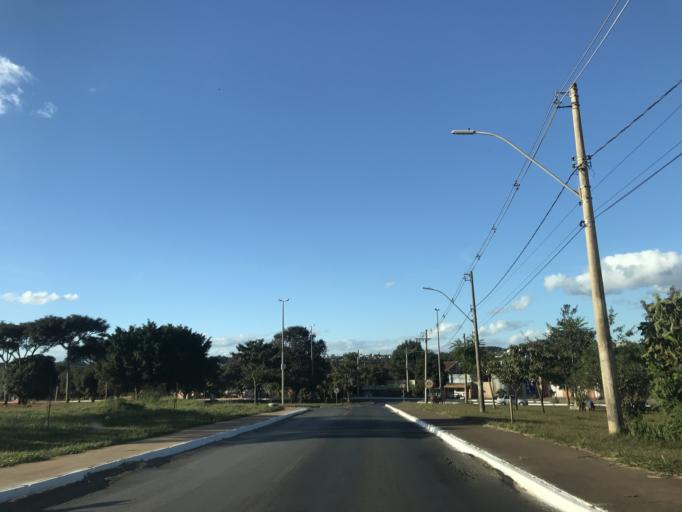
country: BR
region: Federal District
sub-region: Brasilia
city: Brasilia
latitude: -15.8890
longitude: -47.7804
